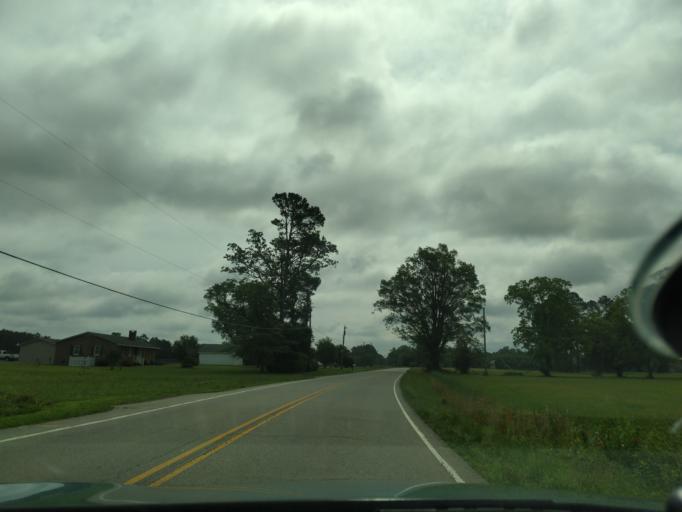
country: US
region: North Carolina
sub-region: Washington County
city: Plymouth
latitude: 35.8762
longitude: -76.6400
